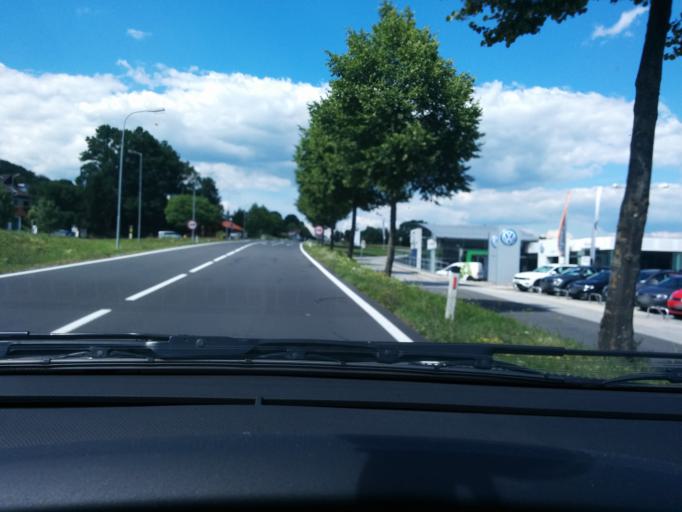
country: AT
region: Styria
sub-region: Politischer Bezirk Hartberg-Fuerstenfeld
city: Hartberg
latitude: 47.2901
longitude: 15.9793
